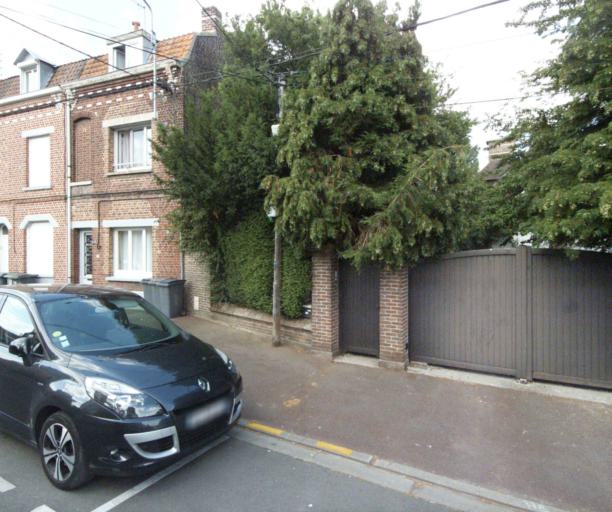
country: FR
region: Nord-Pas-de-Calais
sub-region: Departement du Nord
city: Mouvaux
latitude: 50.6974
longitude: 3.1329
